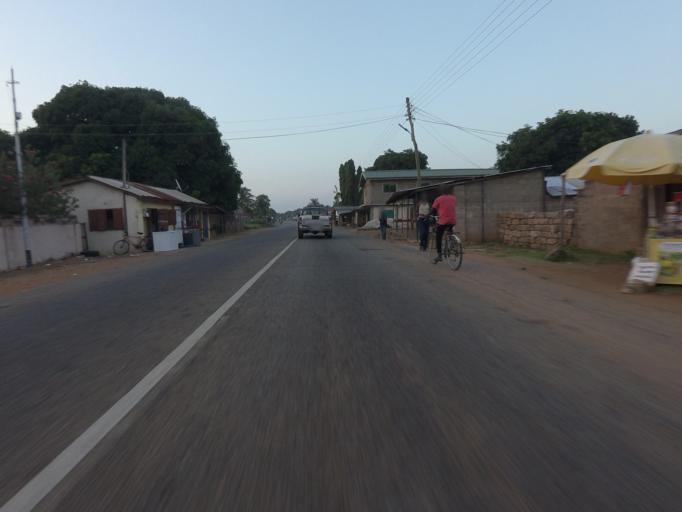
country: GH
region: Volta
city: Keta
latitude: 5.8600
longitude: 0.9778
